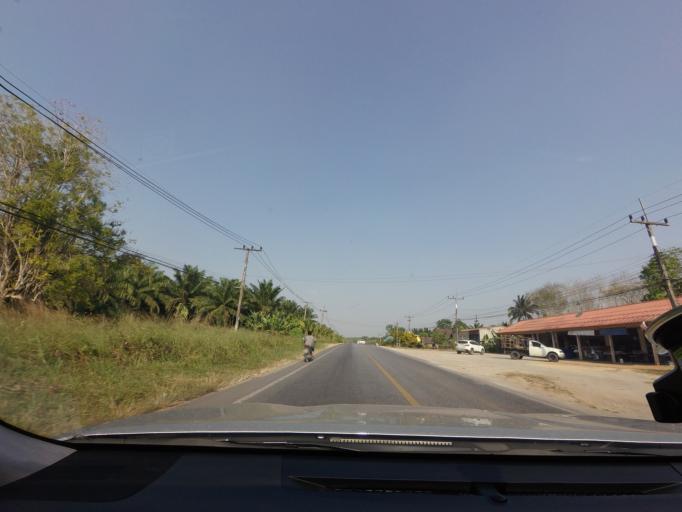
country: TH
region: Surat Thani
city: Chai Buri
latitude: 8.5699
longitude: 99.1206
